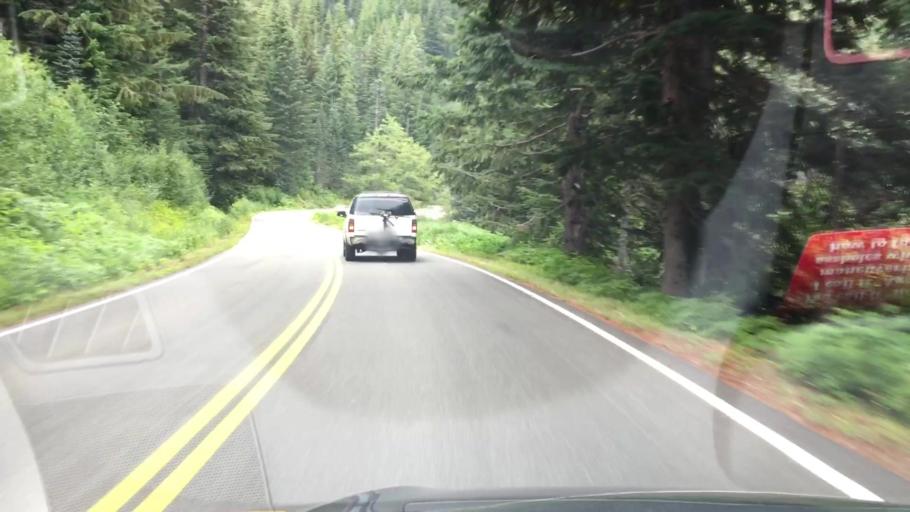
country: US
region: Washington
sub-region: Pierce County
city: Buckley
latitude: 46.7737
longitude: -121.7030
